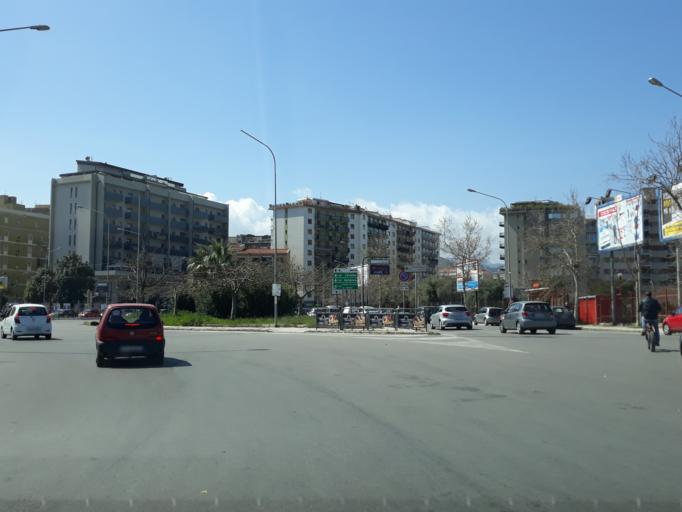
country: IT
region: Sicily
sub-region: Palermo
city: Palermo
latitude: 38.1294
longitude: 13.3291
